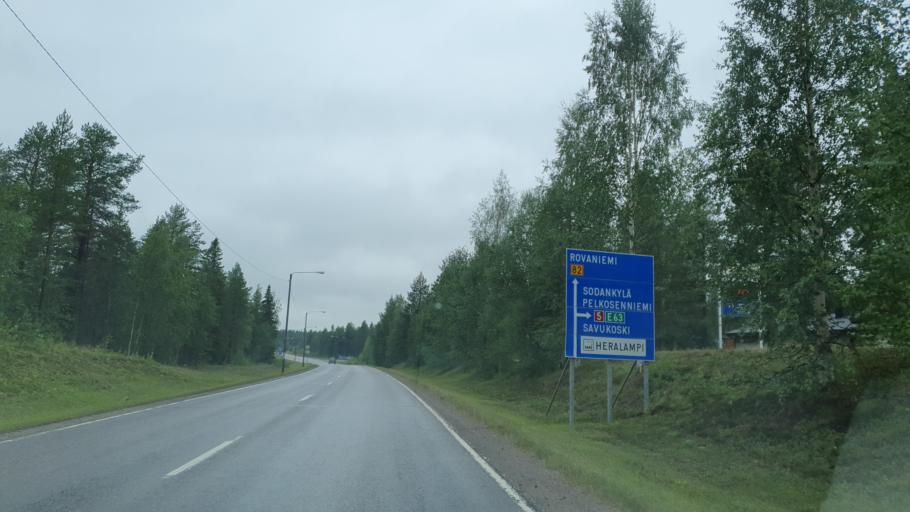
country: FI
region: Lapland
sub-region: Itae-Lappi
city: Kemijaervi
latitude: 66.7200
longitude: 27.3721
